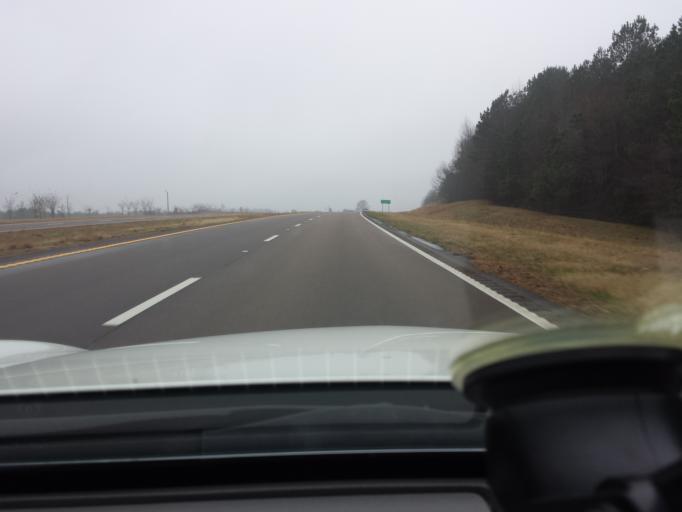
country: US
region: Mississippi
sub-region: Leake County
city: Carthage
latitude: 32.7737
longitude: -89.5279
